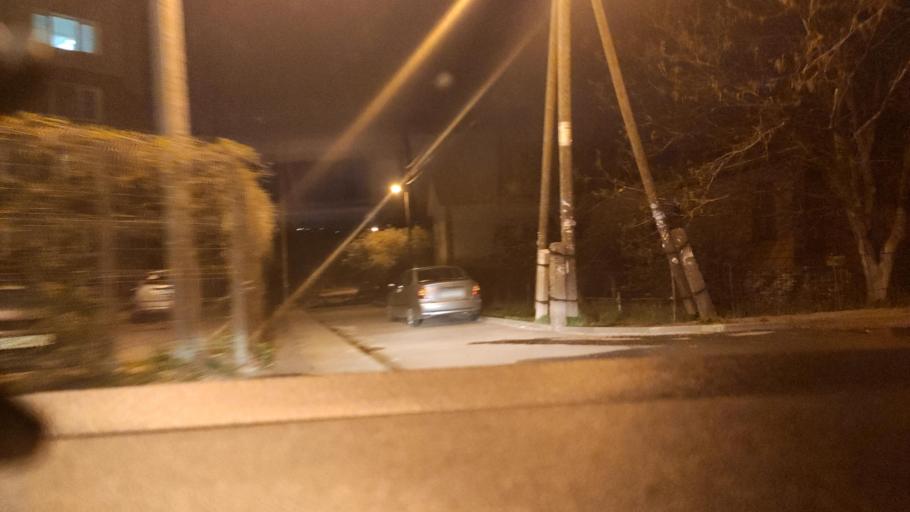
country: RU
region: Voronezj
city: Voronezh
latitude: 51.6753
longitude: 39.1330
